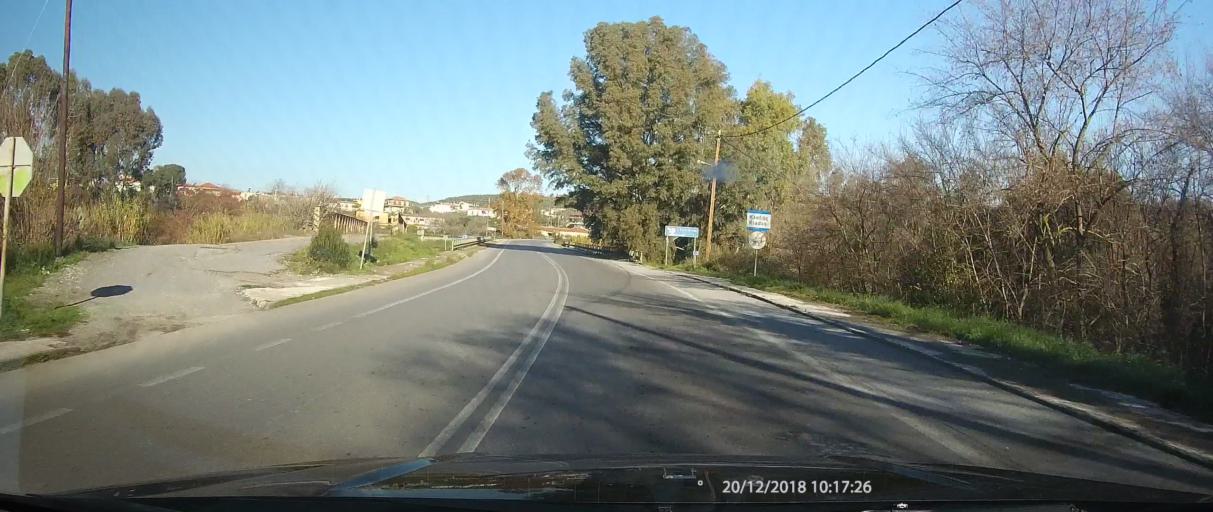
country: GR
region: Peloponnese
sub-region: Nomos Lakonias
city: Sparti
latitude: 37.1066
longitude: 22.4342
